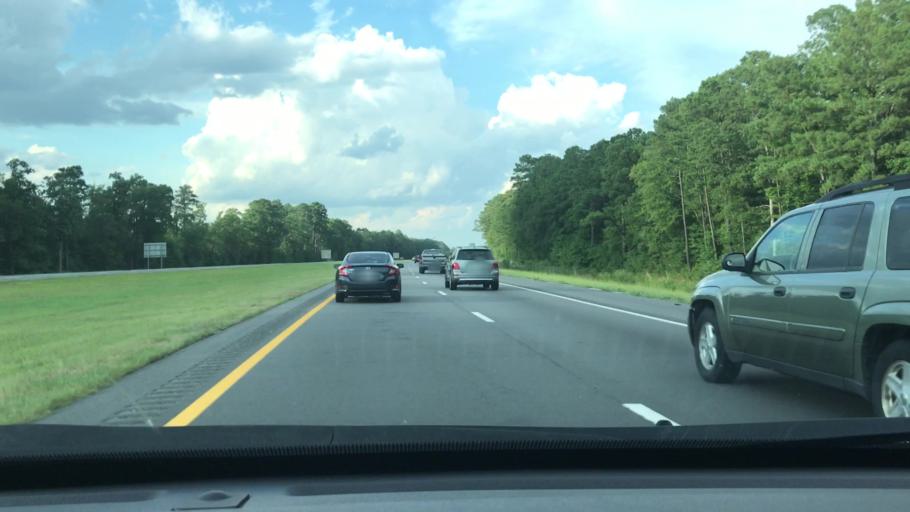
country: US
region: North Carolina
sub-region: Cumberland County
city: Vander
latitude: 35.0123
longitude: -78.8177
